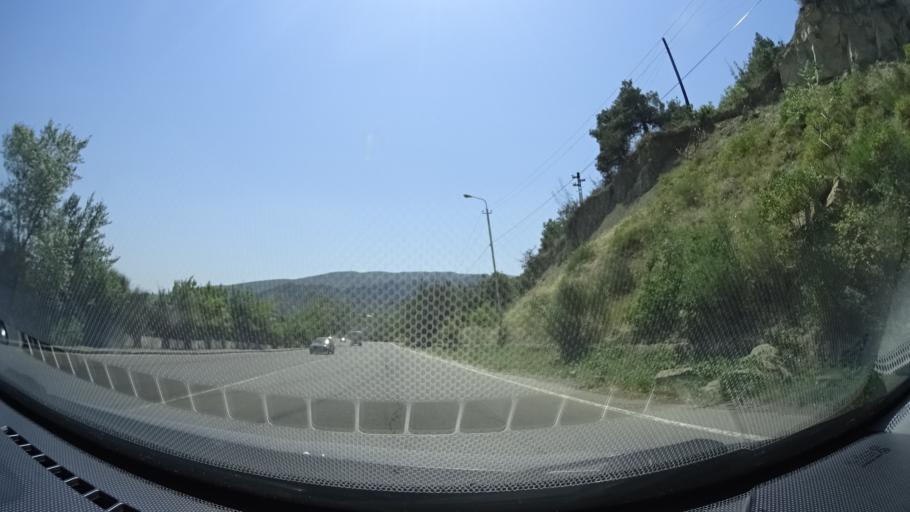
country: GE
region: Mtskheta-Mtianeti
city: Mtskheta
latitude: 41.8541
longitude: 44.7213
